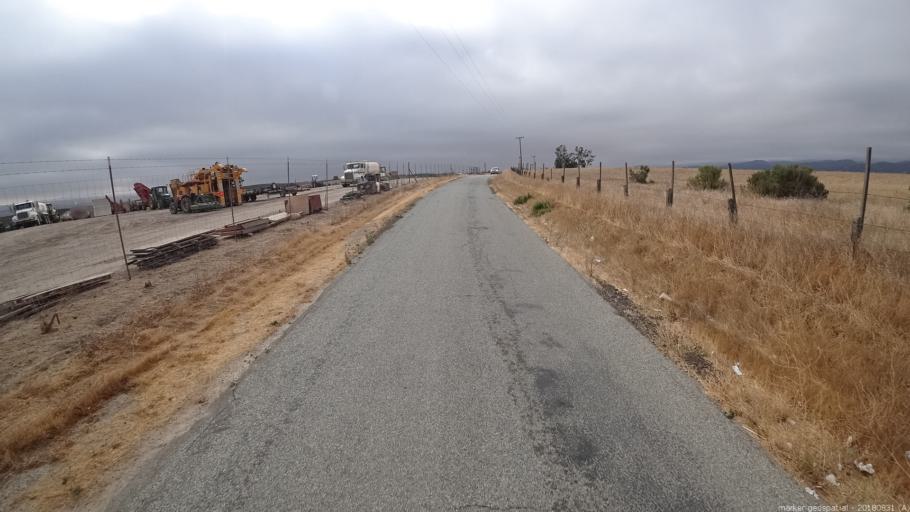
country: US
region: California
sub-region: Monterey County
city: King City
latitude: 36.1325
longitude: -121.0913
